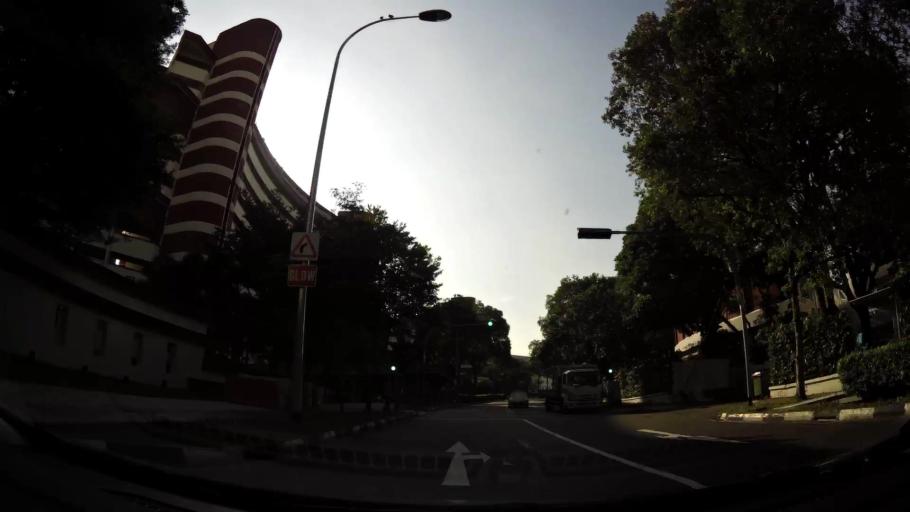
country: SG
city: Singapore
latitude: 1.3260
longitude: 103.9193
